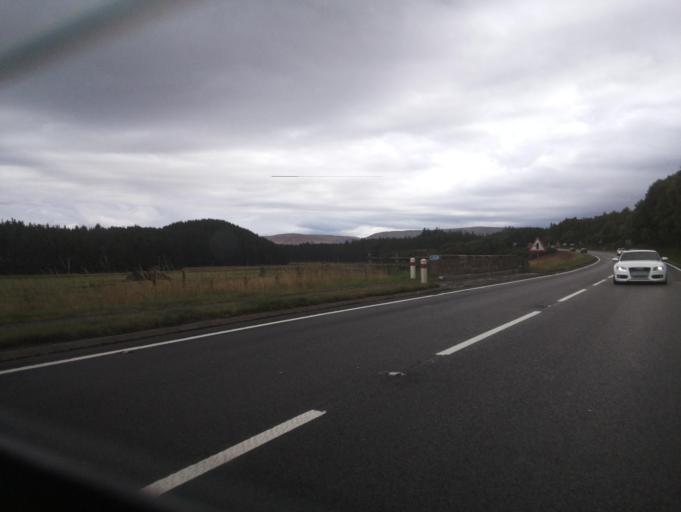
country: GB
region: Scotland
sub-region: Highland
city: Inverness
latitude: 57.3642
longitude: -4.0170
